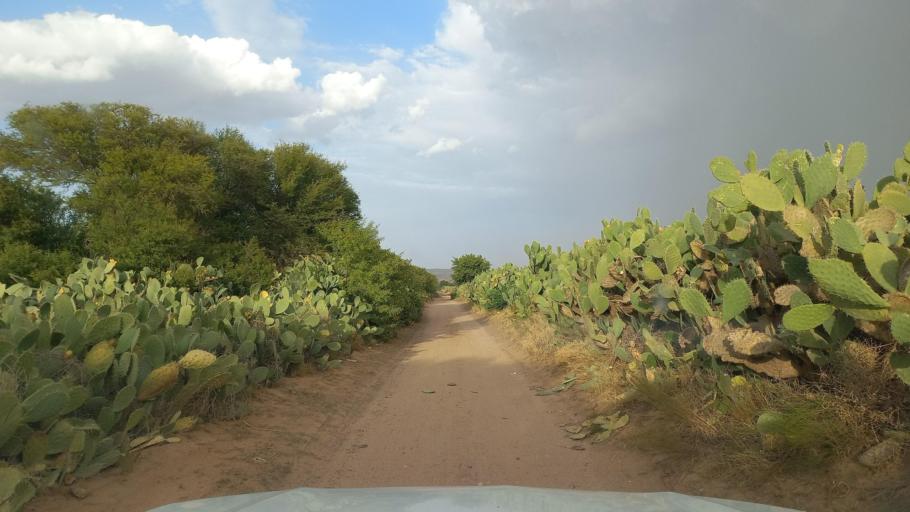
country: TN
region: Al Qasrayn
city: Kasserine
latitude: 35.2821
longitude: 9.0591
